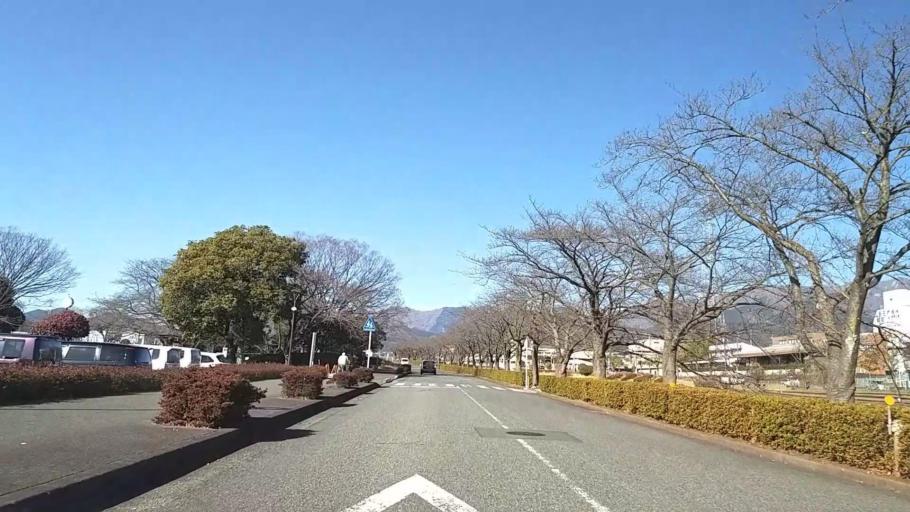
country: JP
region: Kanagawa
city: Hadano
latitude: 35.3816
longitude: 139.2018
